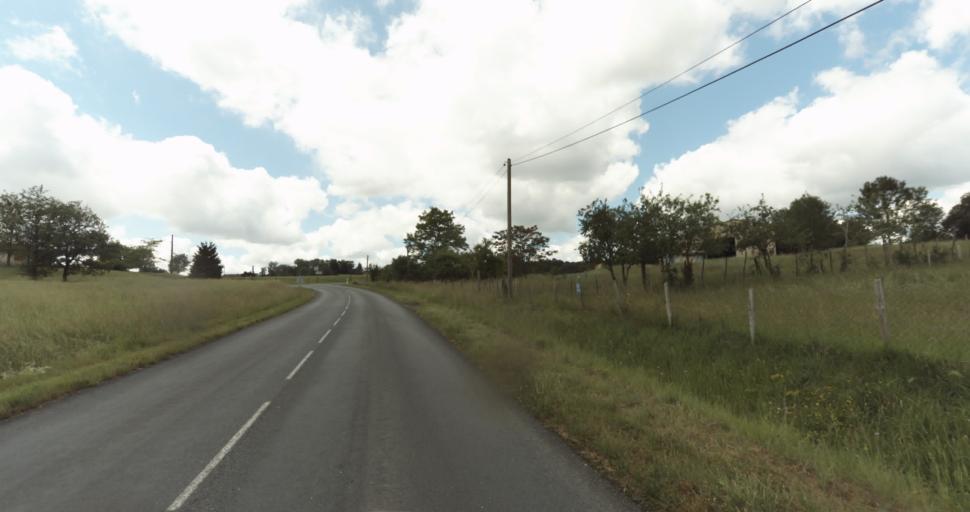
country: FR
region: Aquitaine
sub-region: Departement de la Dordogne
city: Beaumont-du-Perigord
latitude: 44.7402
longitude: 0.7528
